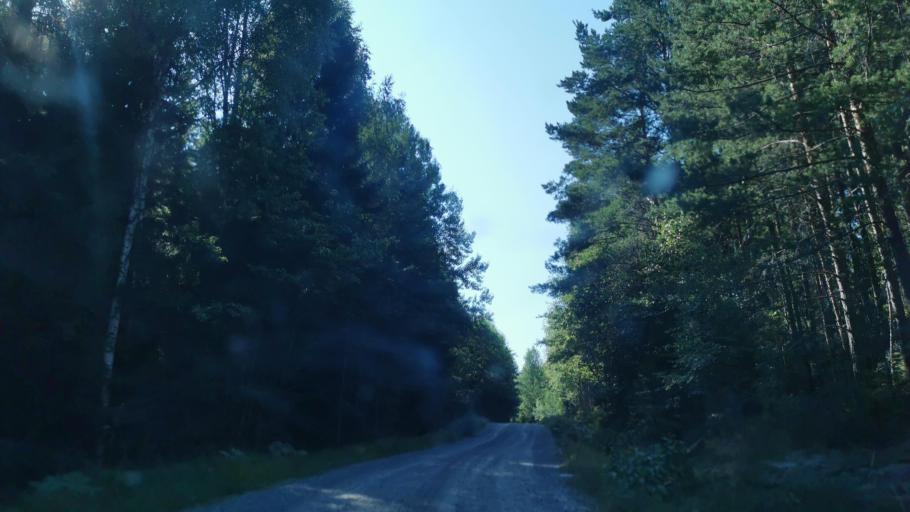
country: SE
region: OEstergoetland
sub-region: Norrkopings Kommun
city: Jursla
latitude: 58.7106
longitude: 16.1771
